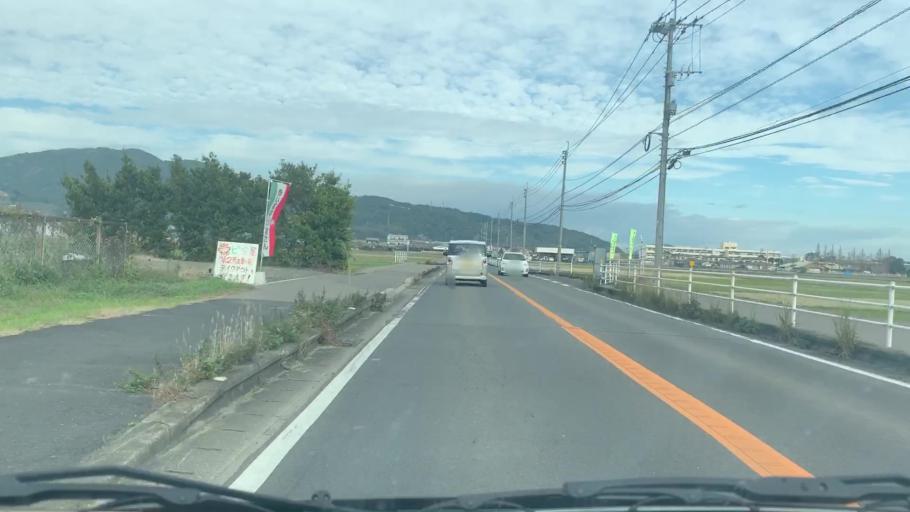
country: JP
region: Saga Prefecture
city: Karatsu
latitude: 33.4000
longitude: 129.9873
